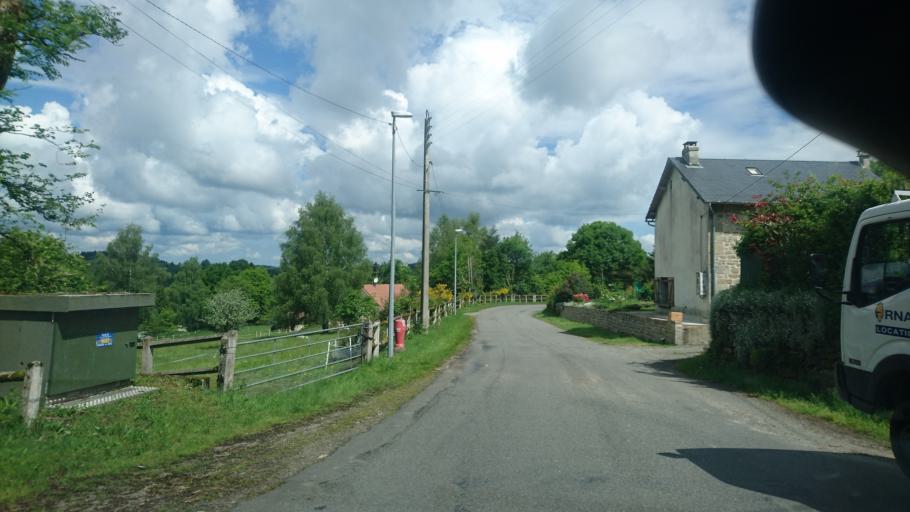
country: FR
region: Limousin
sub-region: Departement de la Haute-Vienne
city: Peyrat-le-Chateau
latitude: 45.7807
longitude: 1.8768
